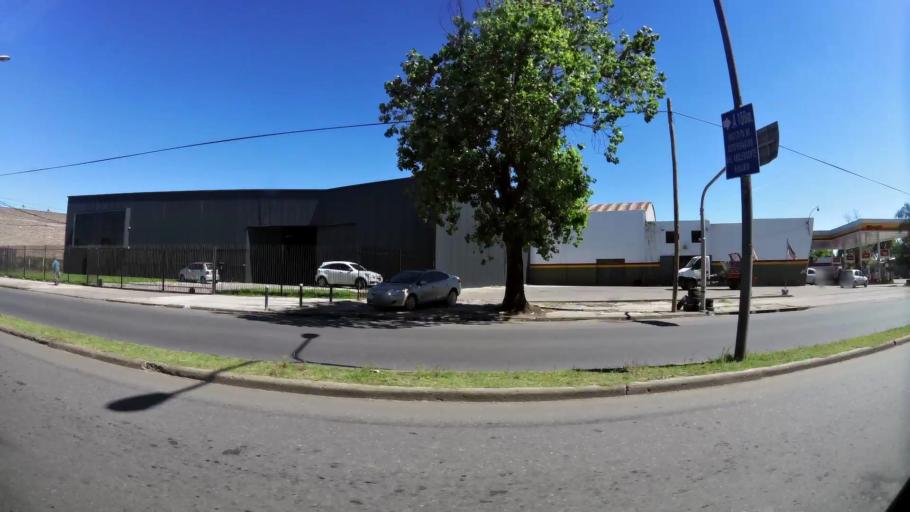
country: AR
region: Santa Fe
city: Perez
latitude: -32.9683
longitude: -60.7121
